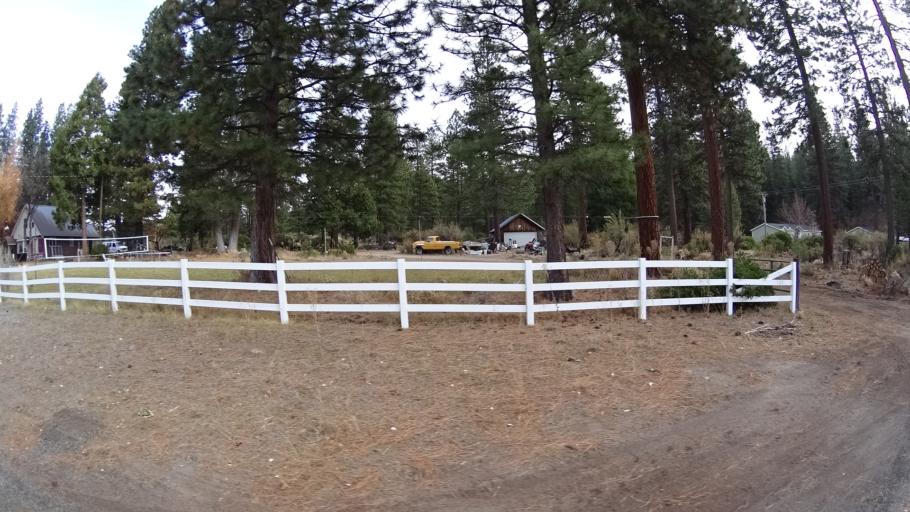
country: US
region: California
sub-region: Siskiyou County
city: Weed
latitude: 41.4456
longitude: -122.3588
